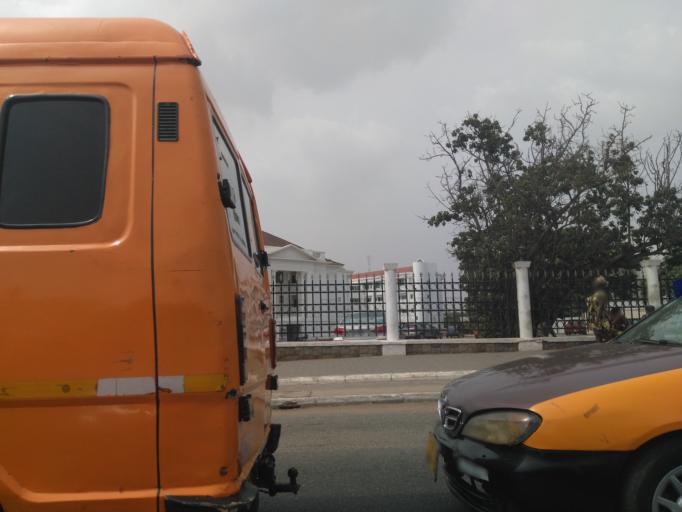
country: GH
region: Greater Accra
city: Accra
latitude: 5.5452
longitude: -0.2037
